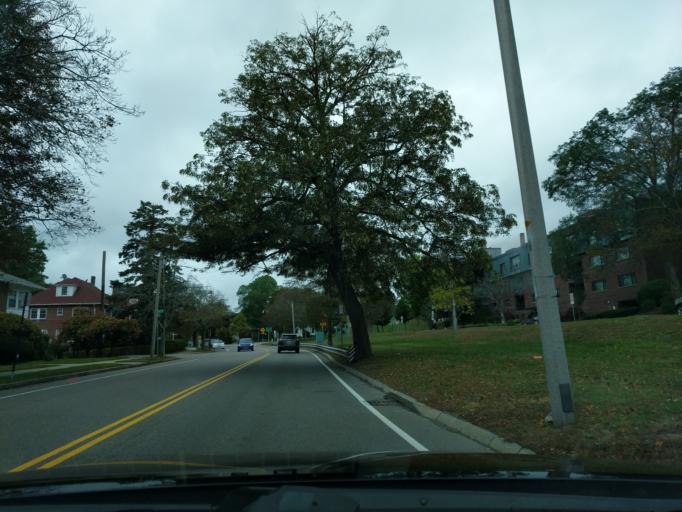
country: US
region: Massachusetts
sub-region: Middlesex County
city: Watertown
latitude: 42.3372
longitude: -71.1737
